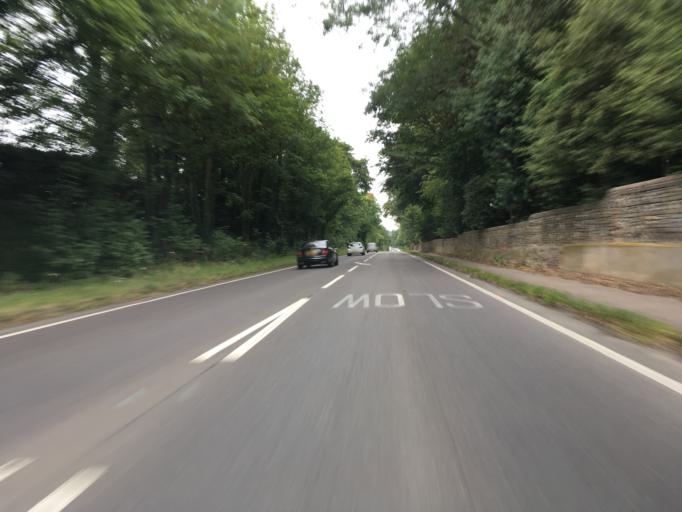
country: GB
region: England
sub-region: Hertfordshire
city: Markyate
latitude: 51.8414
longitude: -0.4661
